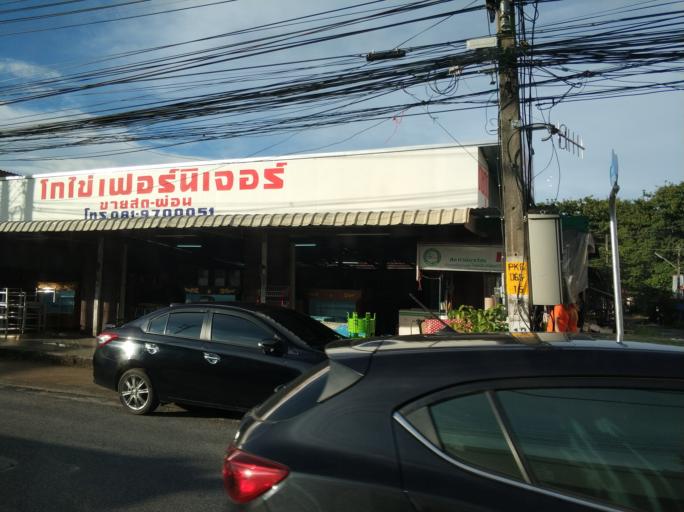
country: TH
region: Phuket
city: Ban Talat Nua
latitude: 7.8847
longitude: 98.3796
